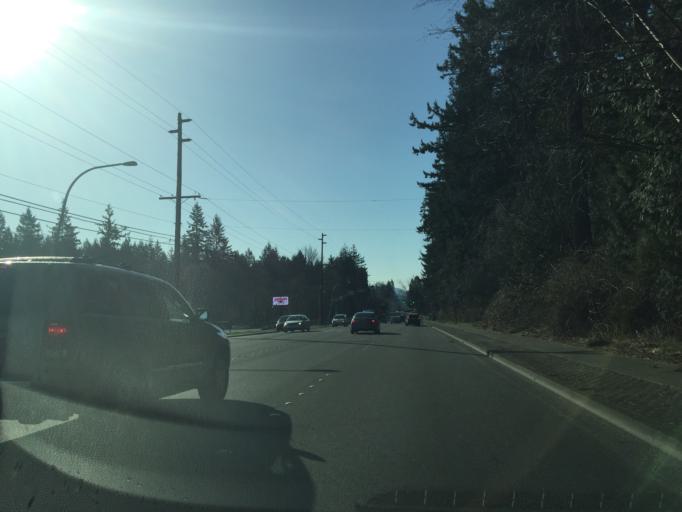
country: US
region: Washington
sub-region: Whatcom County
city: Bellingham
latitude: 48.7783
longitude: -122.4862
